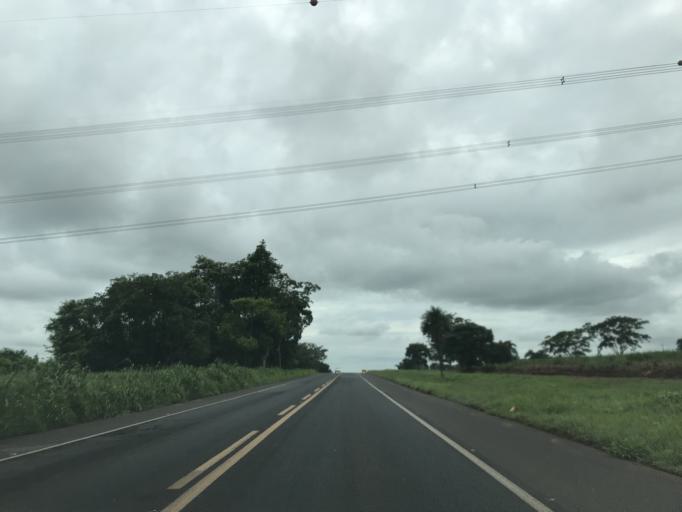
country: BR
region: Sao Paulo
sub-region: Nova Granada
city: Nova Granada
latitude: -20.4281
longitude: -49.2736
